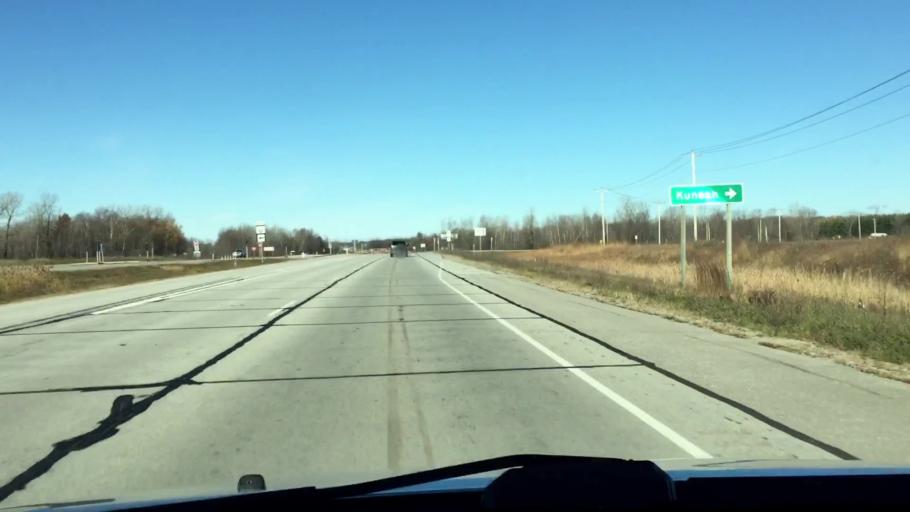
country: US
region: Wisconsin
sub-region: Brown County
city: Oneida
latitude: 44.5834
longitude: -88.1881
